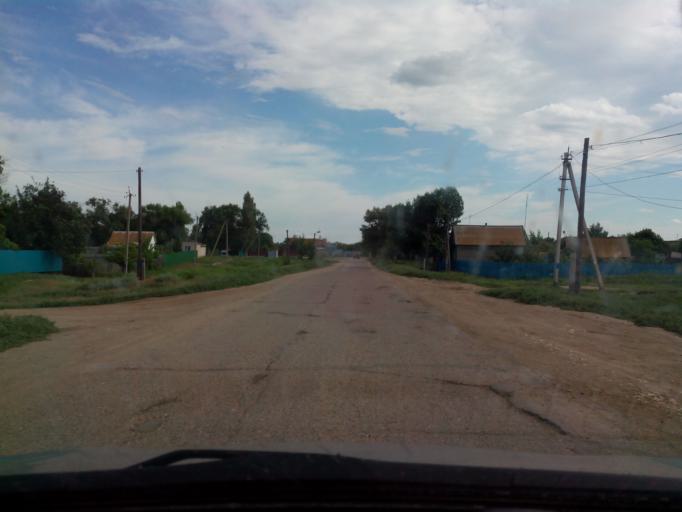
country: RU
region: Volgograd
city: Leninsk
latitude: 48.6694
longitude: 45.3682
